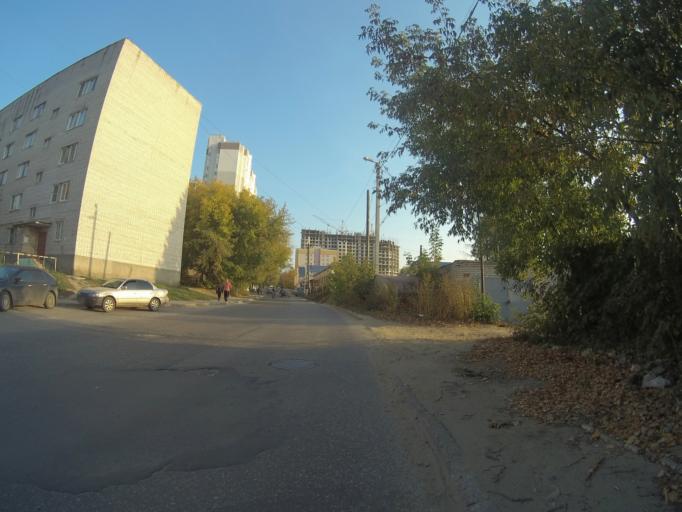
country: RU
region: Vladimir
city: Vladimir
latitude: 56.1205
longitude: 40.3448
